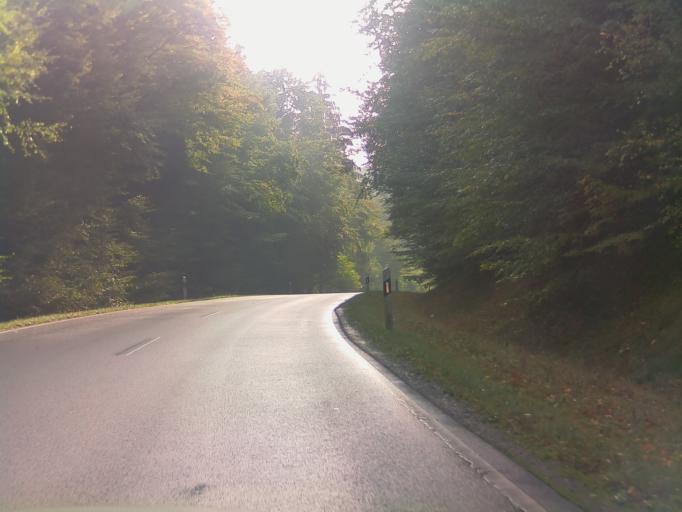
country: DE
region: Hesse
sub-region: Regierungsbezirk Kassel
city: Hosenfeld
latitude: 50.5050
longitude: 9.5218
